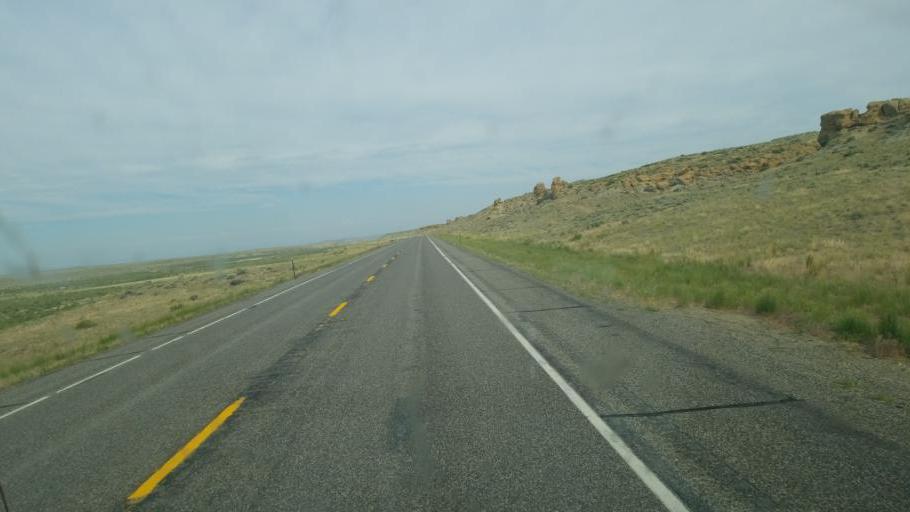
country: US
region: Wyoming
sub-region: Fremont County
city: Riverton
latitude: 43.2215
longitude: -108.0200
